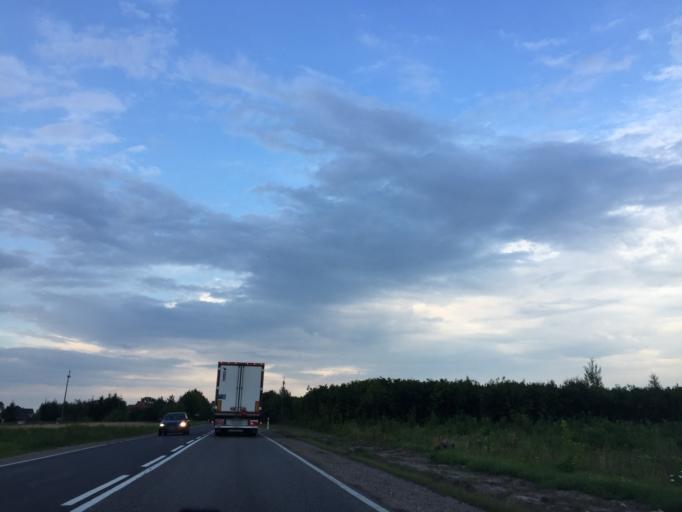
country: PL
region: Masovian Voivodeship
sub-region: Powiat minski
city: Minsk Mazowiecki
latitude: 52.2175
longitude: 21.5387
